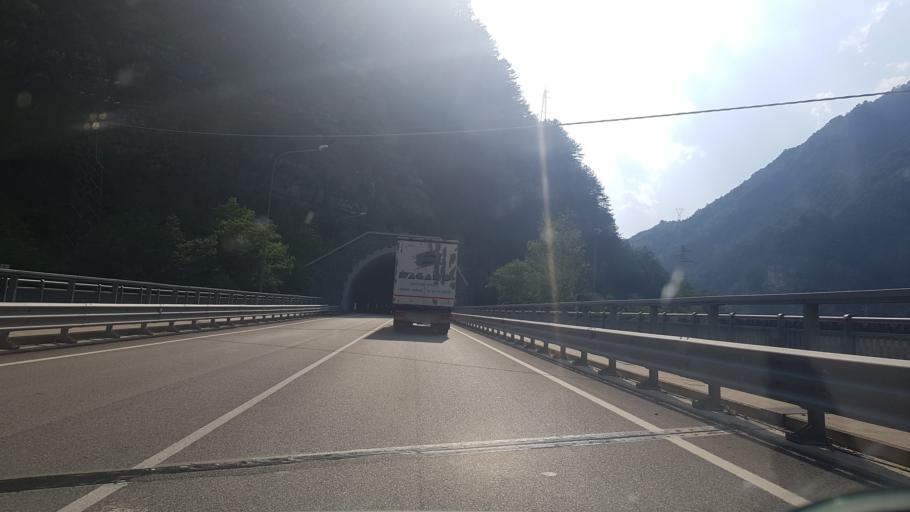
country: IT
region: Friuli Venezia Giulia
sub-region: Provincia di Udine
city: Chiusaforte
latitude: 46.3959
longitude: 13.2697
